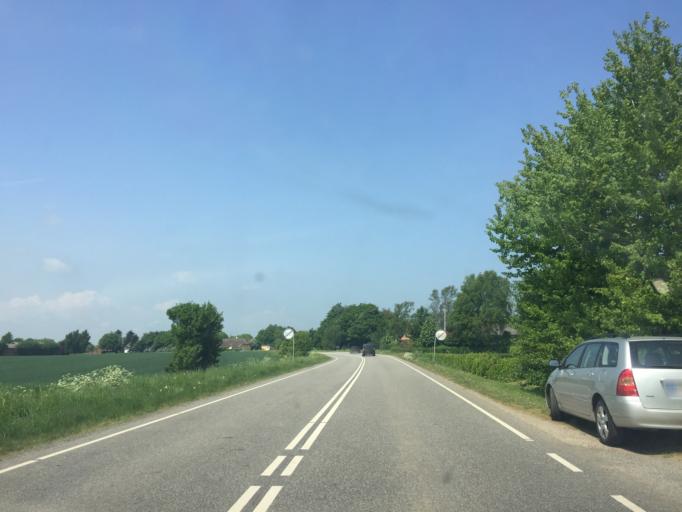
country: DK
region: South Denmark
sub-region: Kolding Kommune
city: Sonder Bjert
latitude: 55.3697
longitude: 9.6007
